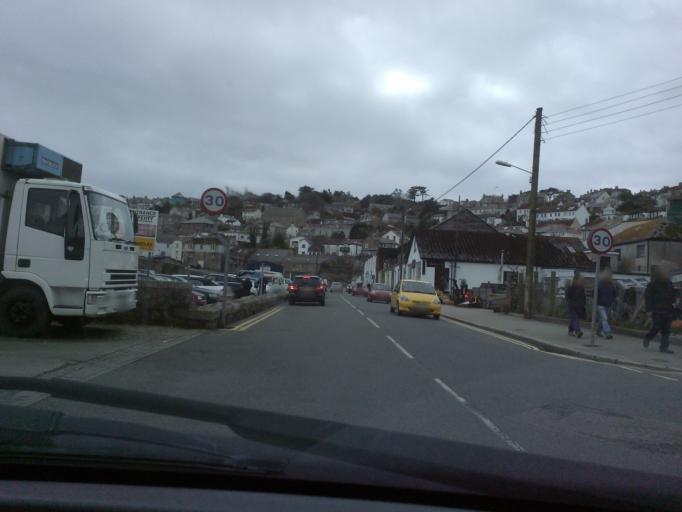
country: GB
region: England
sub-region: Cornwall
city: Penzance
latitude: 50.1046
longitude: -5.5493
